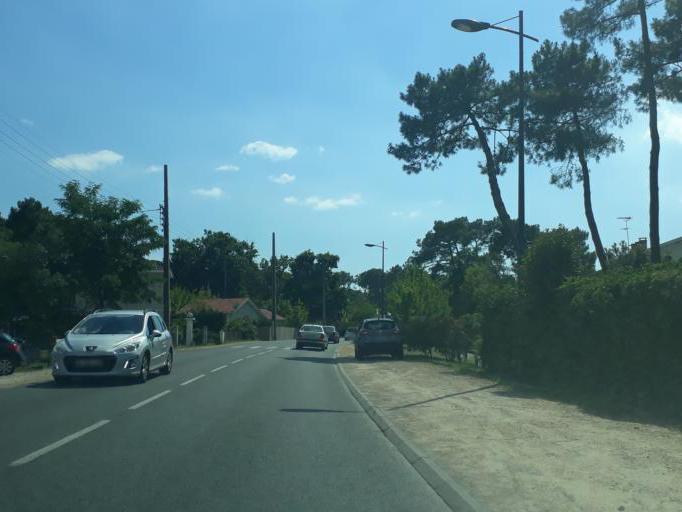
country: FR
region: Aquitaine
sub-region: Departement de la Gironde
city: Ares
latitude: 44.7427
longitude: -1.1827
